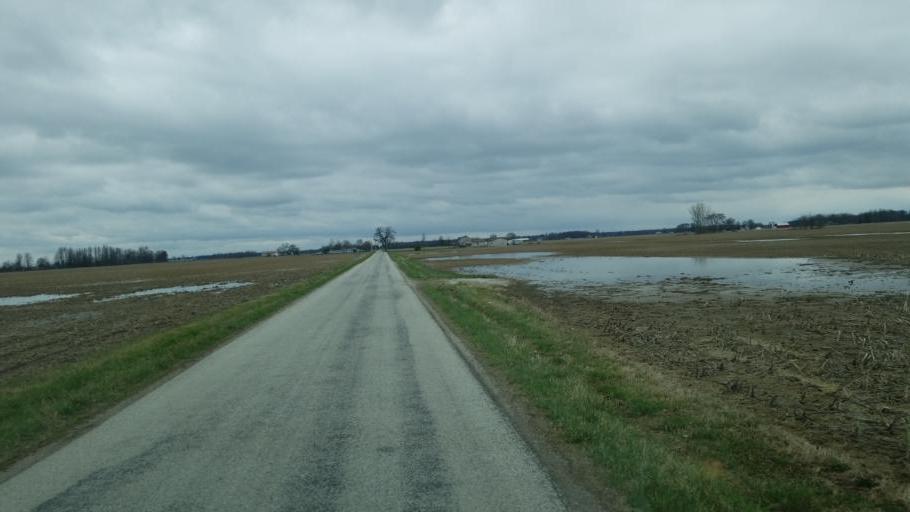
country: US
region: Ohio
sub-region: Marion County
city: Prospect
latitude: 40.4410
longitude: -83.1134
